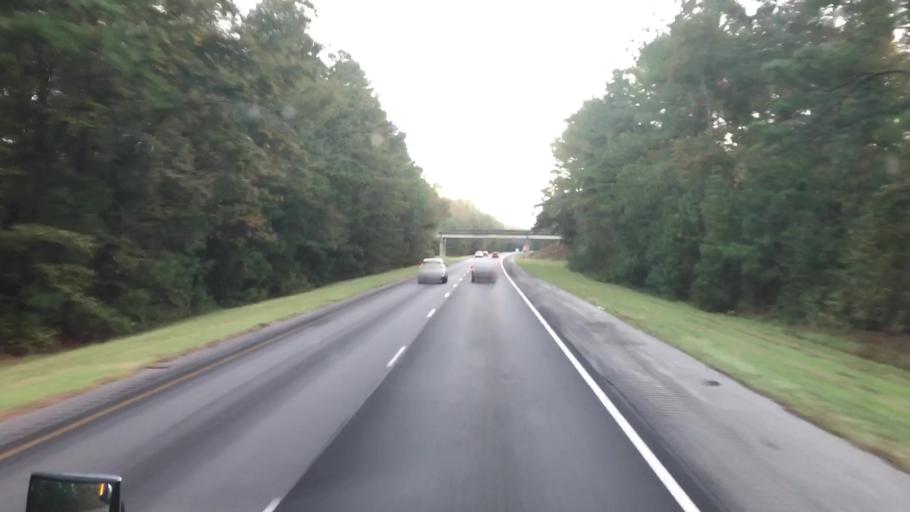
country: US
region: South Carolina
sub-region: Clarendon County
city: Manning
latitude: 33.5652
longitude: -80.3910
